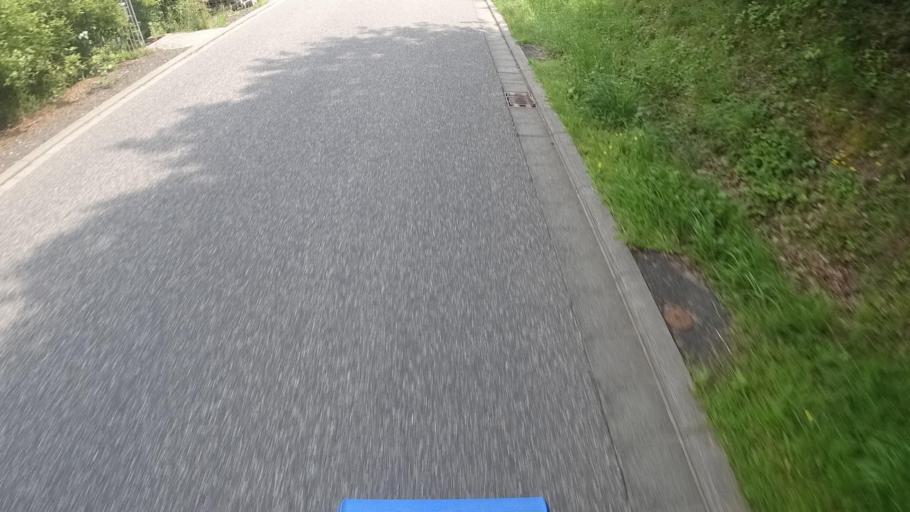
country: DE
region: Rheinland-Pfalz
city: Sankt Katharinen
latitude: 50.5847
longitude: 7.3674
